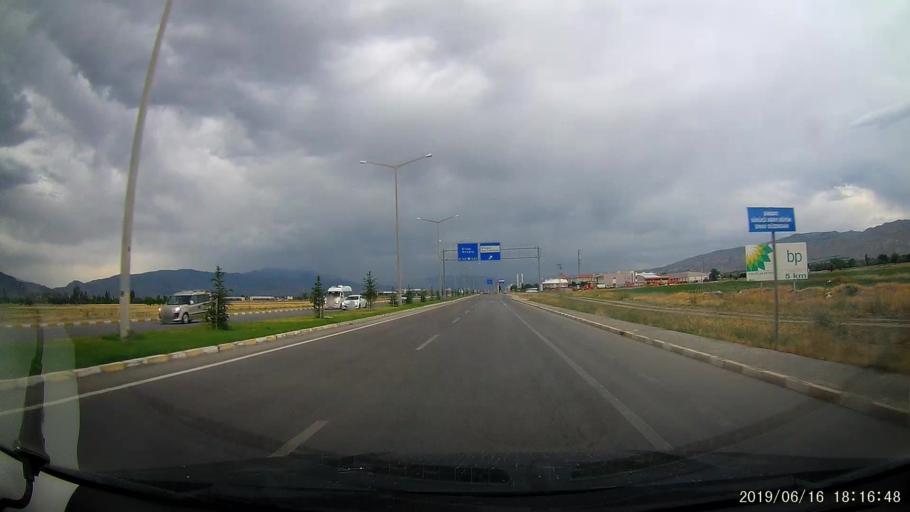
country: TR
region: Erzincan
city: Erzincan
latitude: 39.7306
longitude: 39.5425
